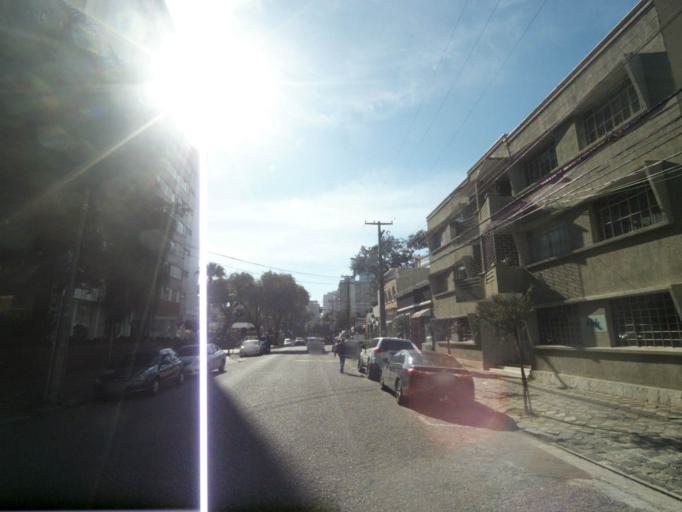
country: BR
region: Parana
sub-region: Curitiba
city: Curitiba
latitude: -25.4387
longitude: -49.2846
